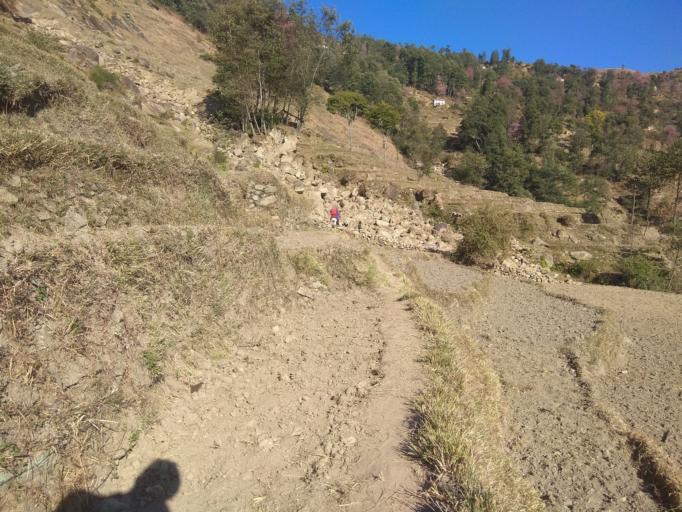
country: NP
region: Far Western
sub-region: Seti Zone
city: Achham
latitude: 29.2563
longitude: 81.6394
